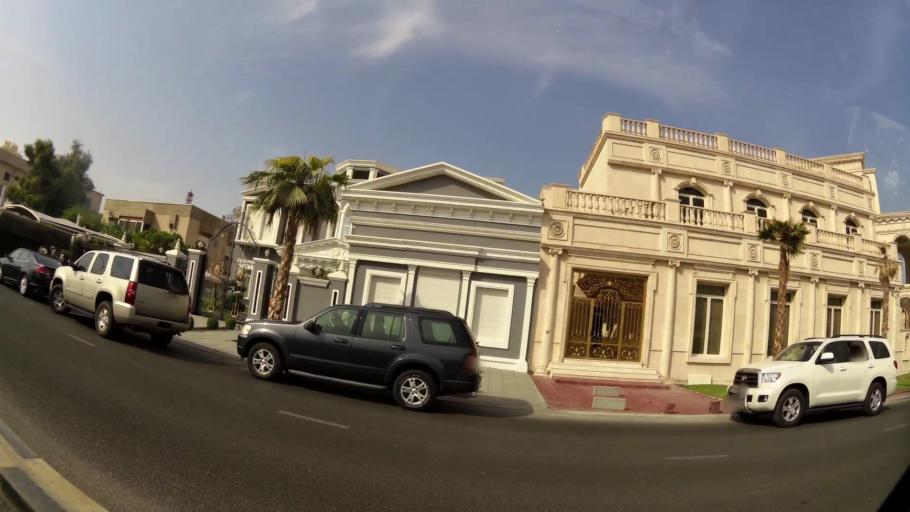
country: KW
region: Al Farwaniyah
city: Al Farwaniyah
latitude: 29.3106
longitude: 47.9657
